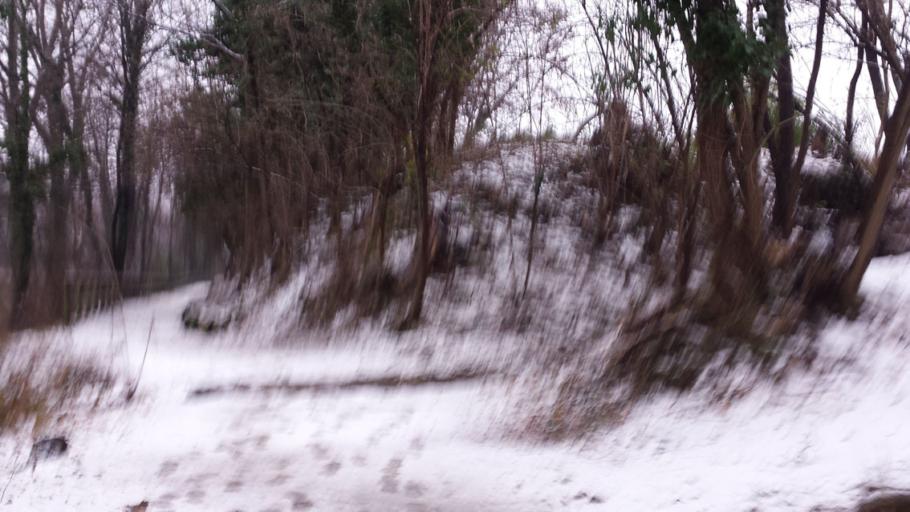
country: IT
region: Veneto
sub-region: Provincia di Vicenza
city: Pove del Grappa
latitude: 45.7868
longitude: 11.7241
